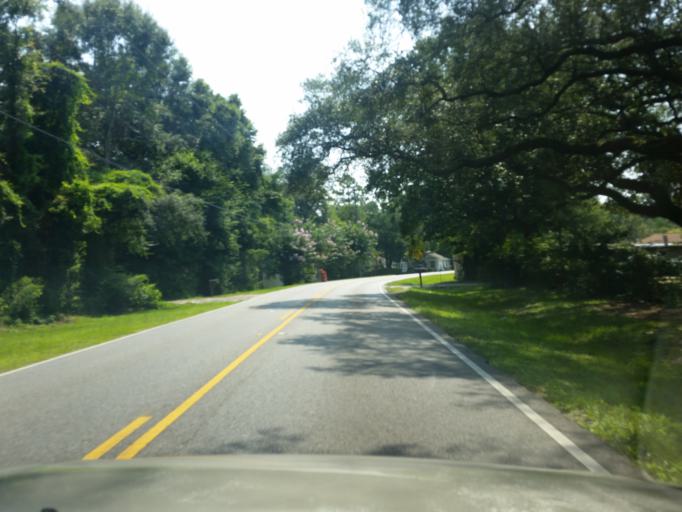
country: US
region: Florida
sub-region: Escambia County
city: Ferry Pass
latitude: 30.5188
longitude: -87.2312
